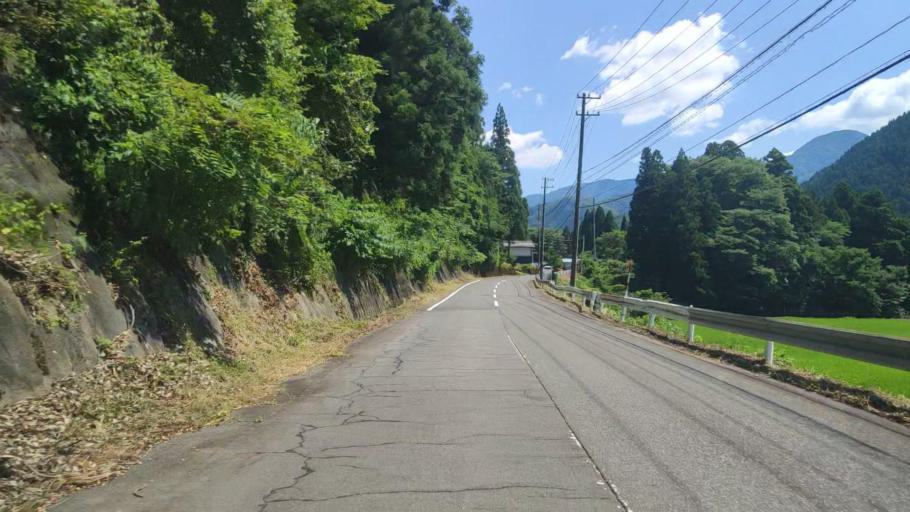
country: JP
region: Gifu
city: Godo
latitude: 35.6727
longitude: 136.5762
